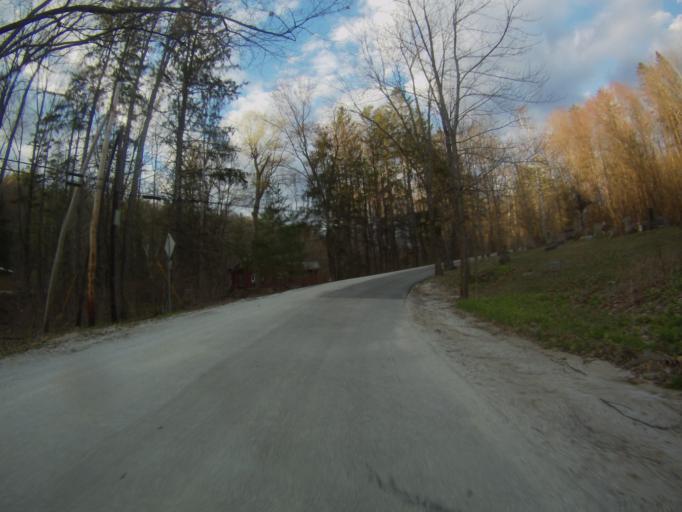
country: US
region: Vermont
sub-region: Rutland County
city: Brandon
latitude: 43.8499
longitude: -73.0217
